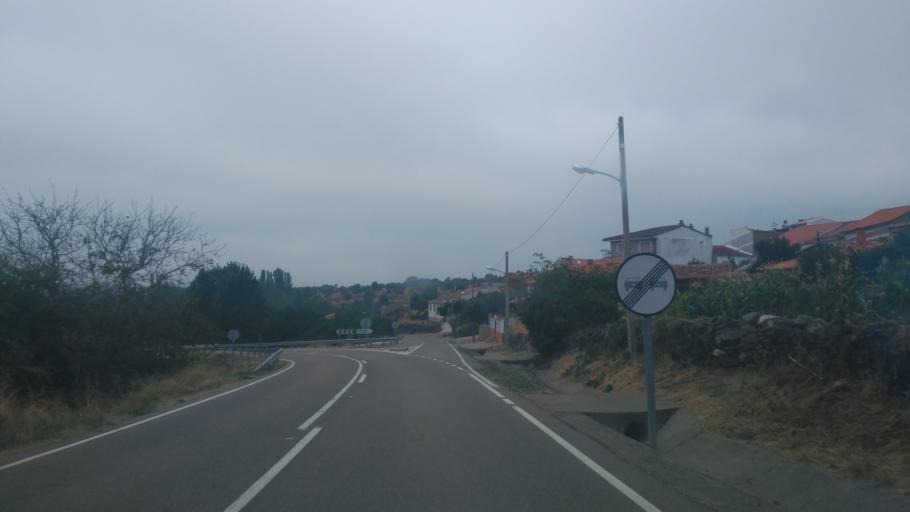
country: ES
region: Castille and Leon
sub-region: Provincia de Salamanca
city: Cereceda de la Sierra
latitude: 40.5649
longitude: -6.0913
